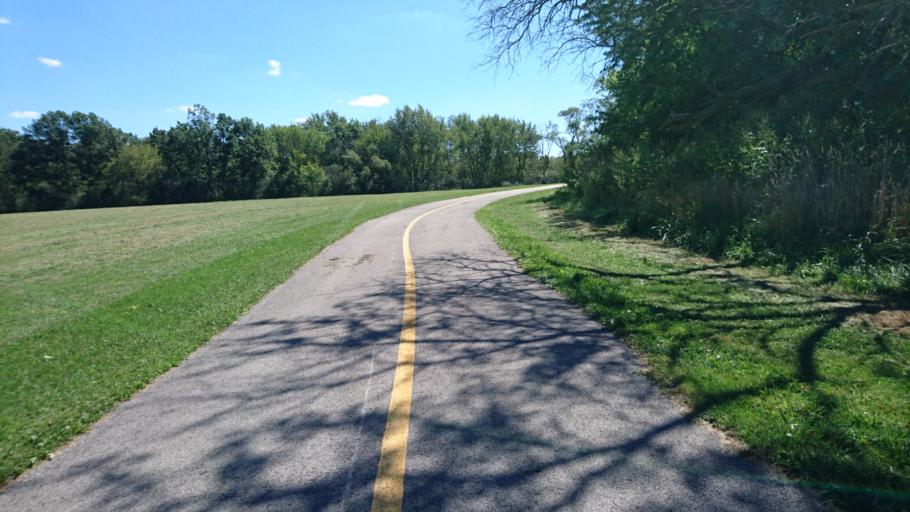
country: US
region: Illinois
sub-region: Cook County
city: Chicago Heights
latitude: 41.5195
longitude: -87.6319
